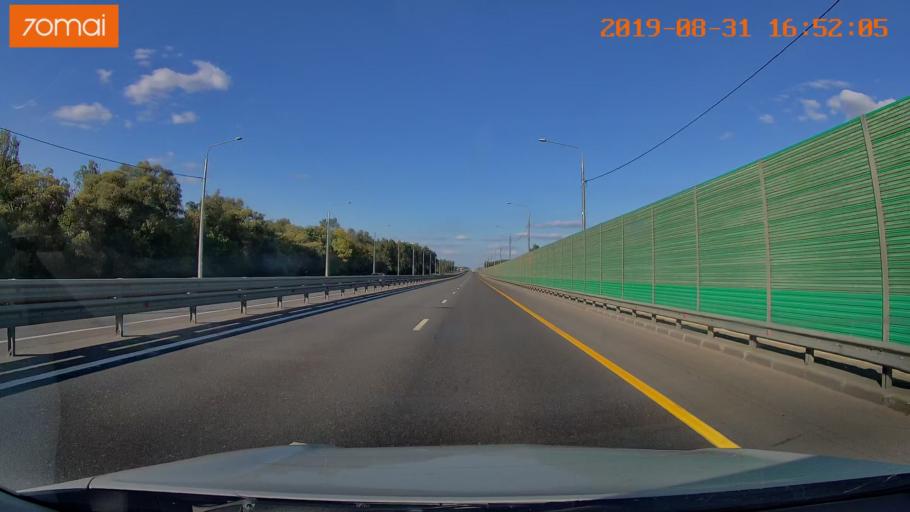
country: RU
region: Kaluga
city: Pyatovskiy
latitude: 54.7363
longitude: 36.1845
